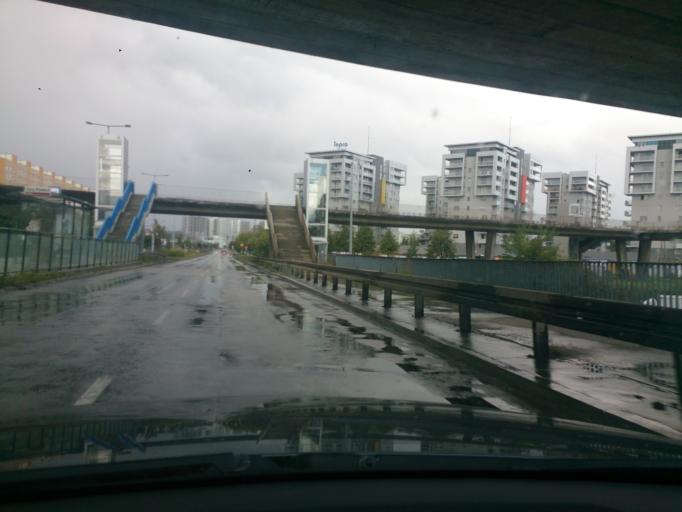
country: PL
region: Pomeranian Voivodeship
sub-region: Gdansk
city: Gdansk
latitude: 54.3945
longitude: 18.6021
